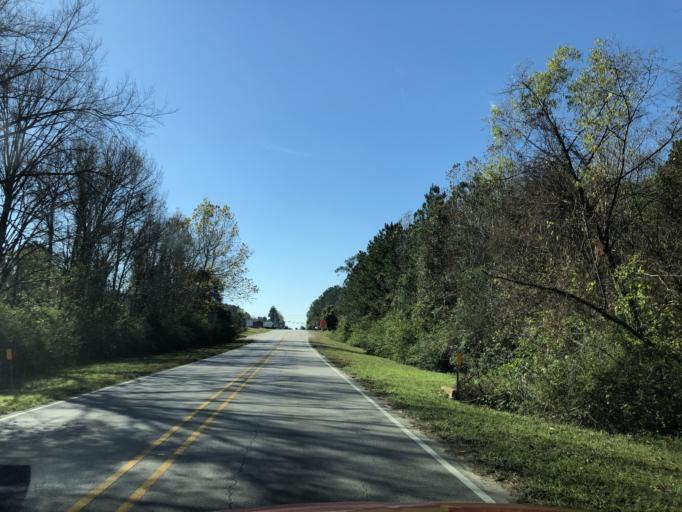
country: US
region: Texas
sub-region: Montgomery County
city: Splendora
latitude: 30.2372
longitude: -95.1601
